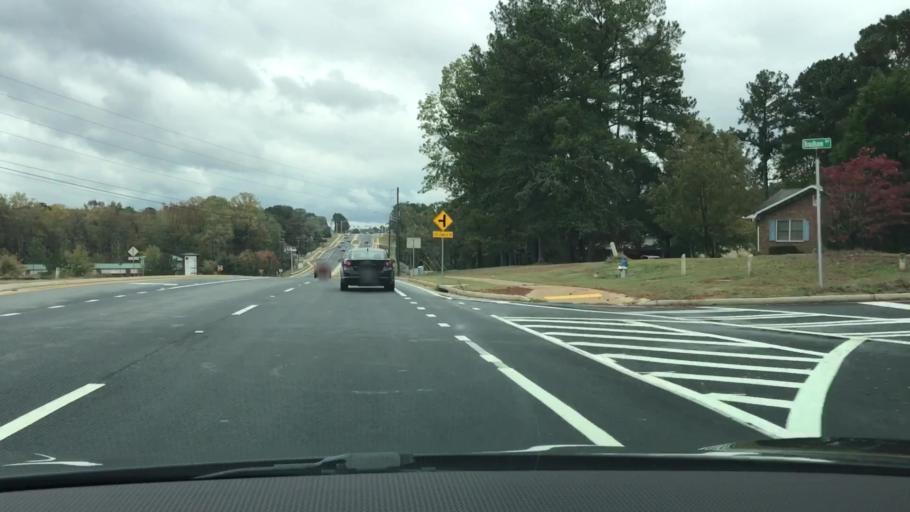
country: US
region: Georgia
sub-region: Oconee County
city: Watkinsville
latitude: 33.8788
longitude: -83.4514
